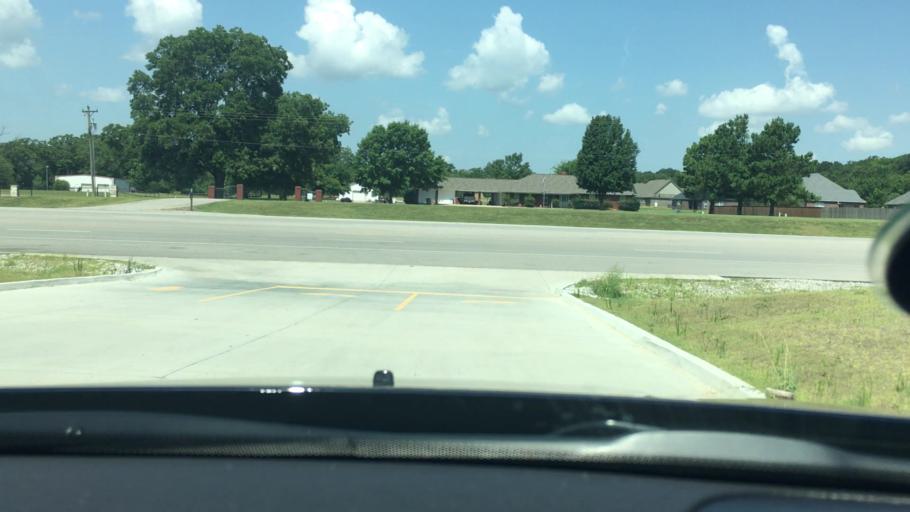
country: US
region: Oklahoma
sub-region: Bryan County
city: Durant
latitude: 34.0428
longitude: -96.3754
